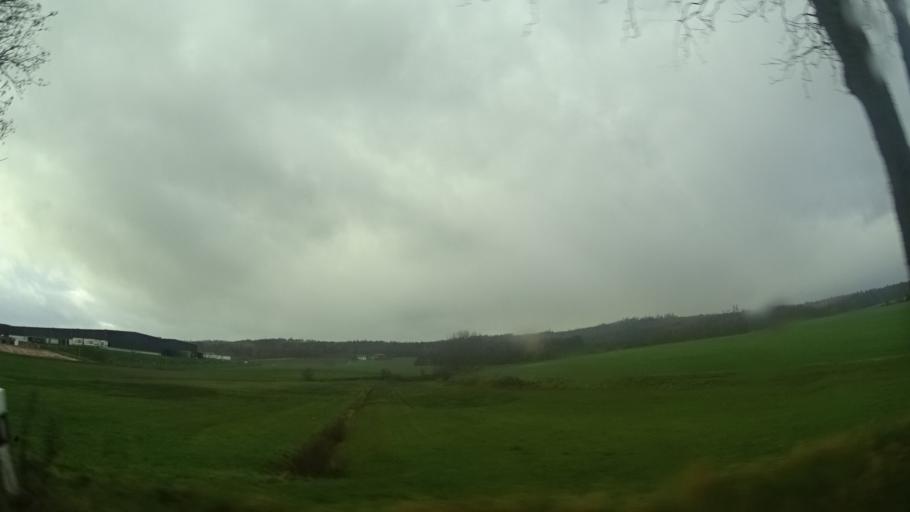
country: DE
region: Hesse
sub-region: Regierungsbezirk Kassel
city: Neuhof
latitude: 50.4708
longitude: 9.6423
